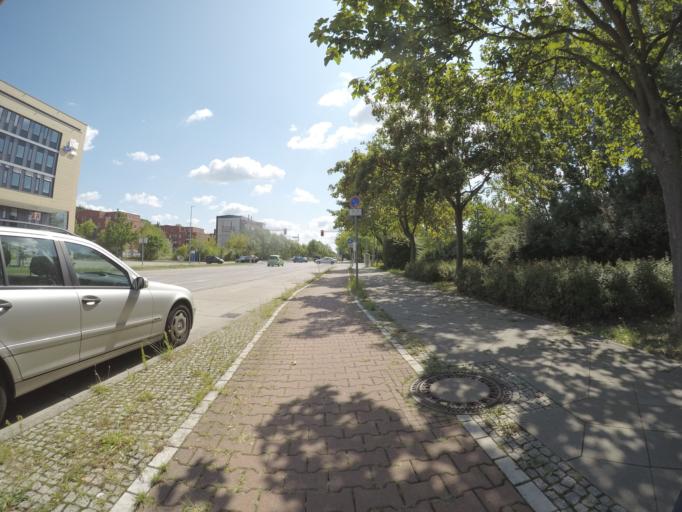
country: DE
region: Berlin
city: Biesdorf
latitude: 52.5195
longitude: 13.5639
